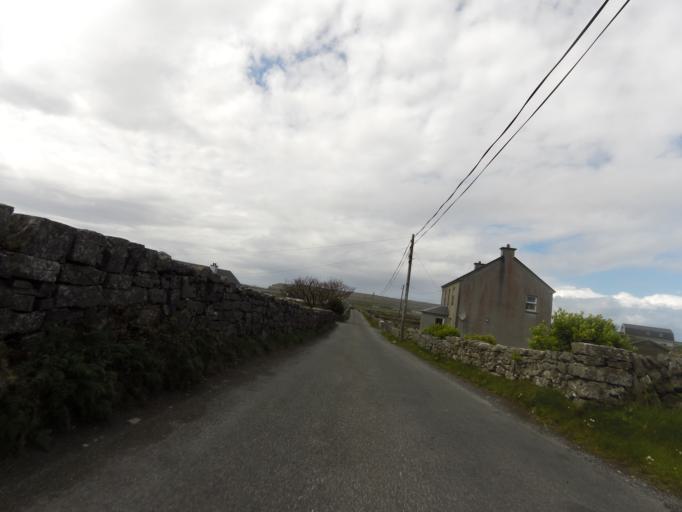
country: IE
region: Connaught
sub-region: County Galway
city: Clifden
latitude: 53.1309
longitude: -9.7364
